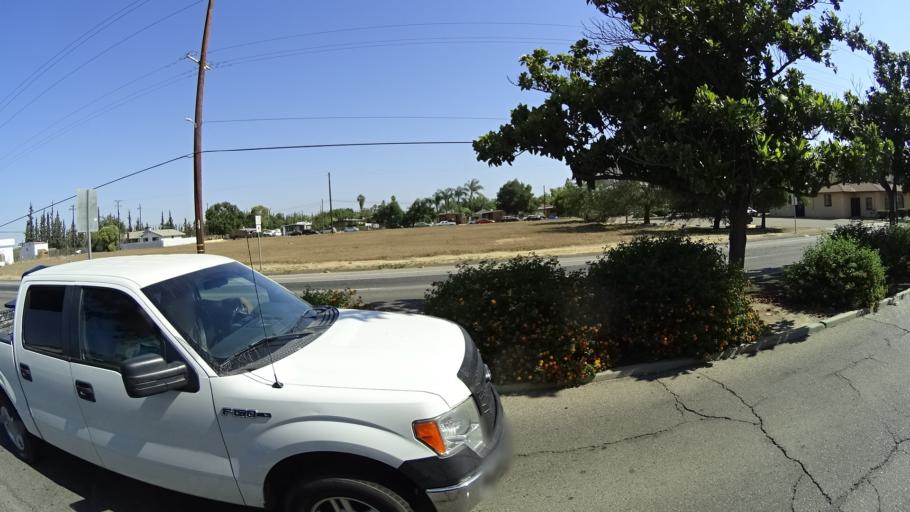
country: US
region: California
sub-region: Fresno County
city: Fresno
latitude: 36.7069
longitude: -119.7989
